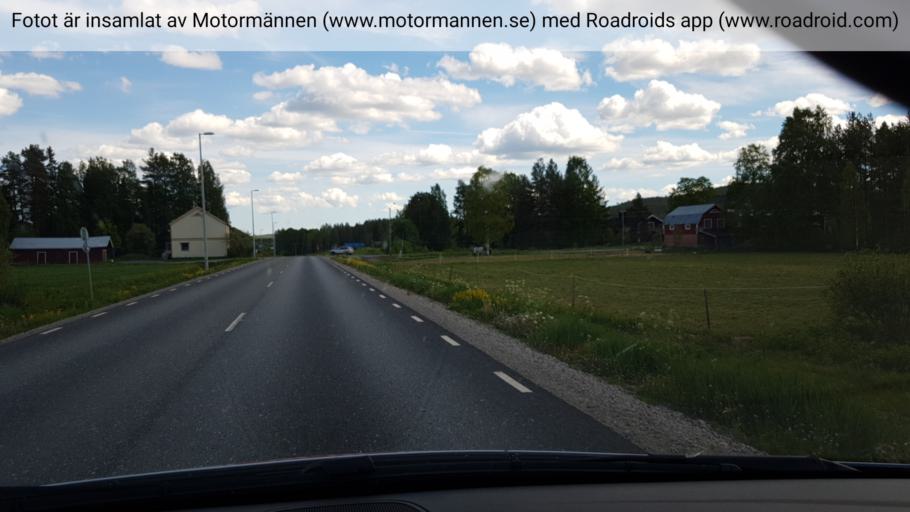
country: SE
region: Vaesterbotten
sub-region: Skelleftea Kommun
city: Forsbacka
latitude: 64.6868
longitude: 20.5229
